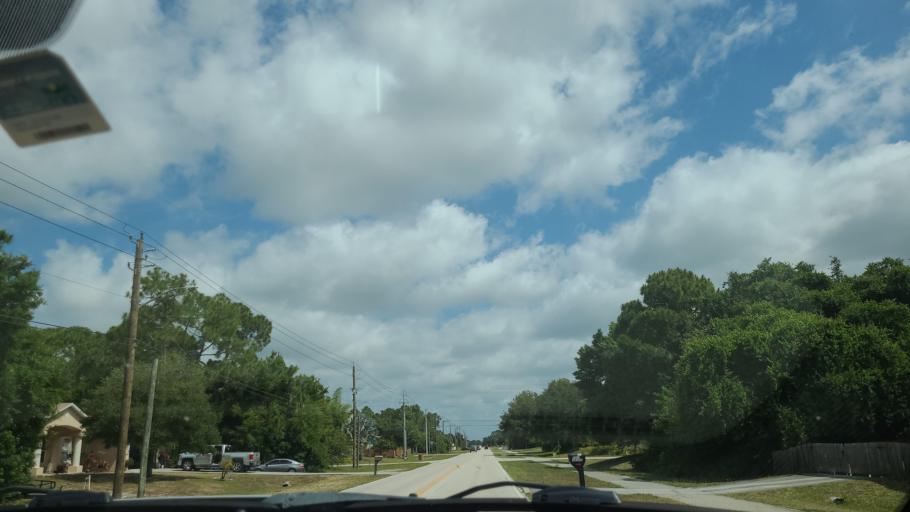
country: US
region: Florida
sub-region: Brevard County
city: June Park
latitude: 28.0093
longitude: -80.6968
